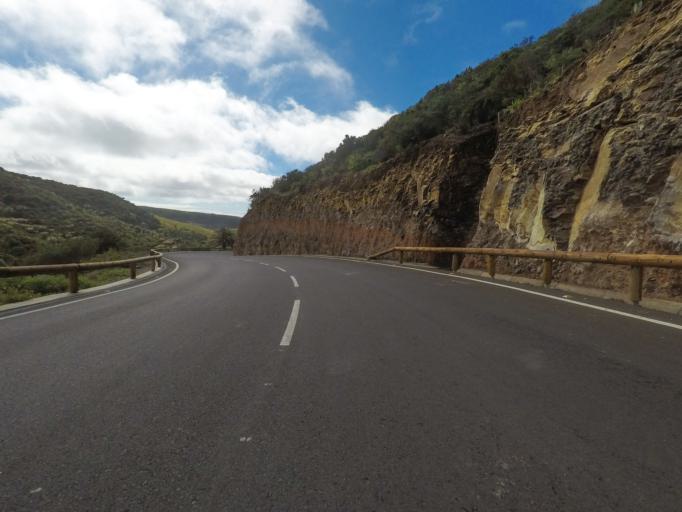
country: ES
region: Canary Islands
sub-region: Provincia de Santa Cruz de Tenerife
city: Vallehermosa
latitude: 28.1425
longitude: -17.3083
